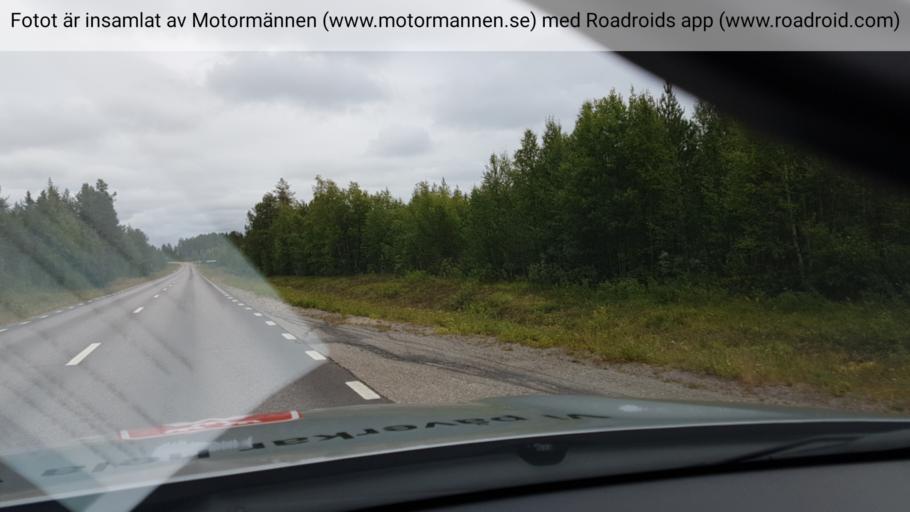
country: SE
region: Norrbotten
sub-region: Gallivare Kommun
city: Gaellivare
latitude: 67.0682
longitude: 21.3086
